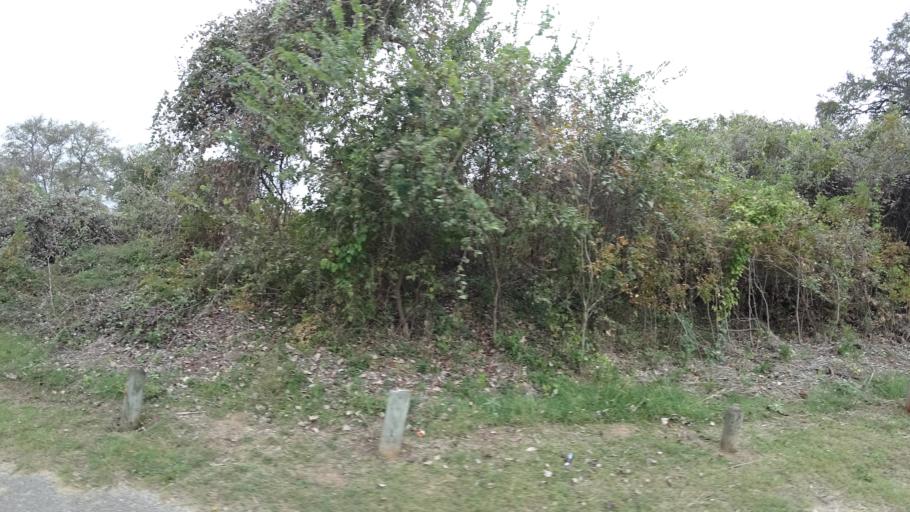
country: US
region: Texas
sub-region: Travis County
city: Bee Cave
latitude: 30.3380
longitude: -97.9036
